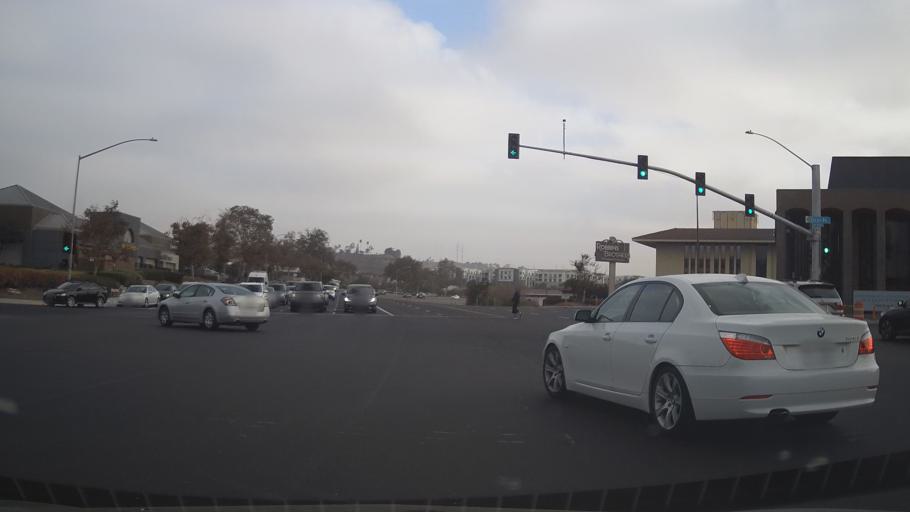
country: US
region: California
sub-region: San Diego County
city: San Diego
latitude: 32.7724
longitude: -117.1571
